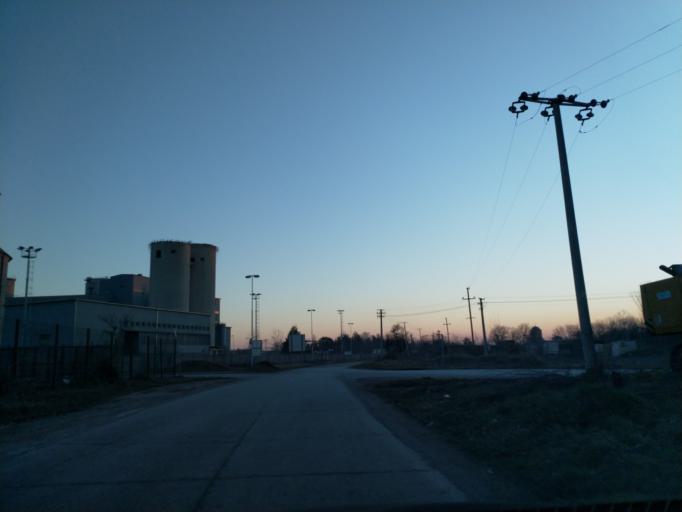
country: RS
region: Central Serbia
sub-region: Pomoravski Okrug
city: Paracin
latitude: 43.9110
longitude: 21.5093
